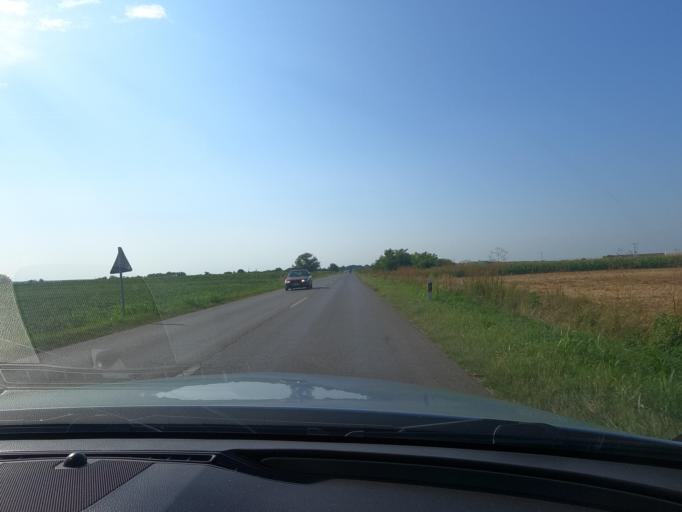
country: RS
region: Autonomna Pokrajina Vojvodina
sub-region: Juznobacki Okrug
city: Kovilj
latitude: 45.2843
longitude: 19.9718
